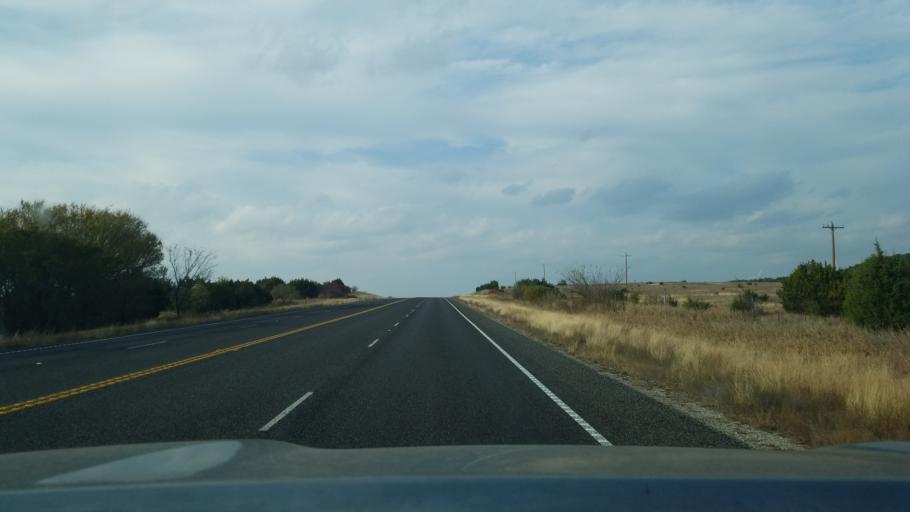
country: US
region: Texas
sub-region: Mills County
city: Goldthwaite
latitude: 31.3274
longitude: -98.4924
